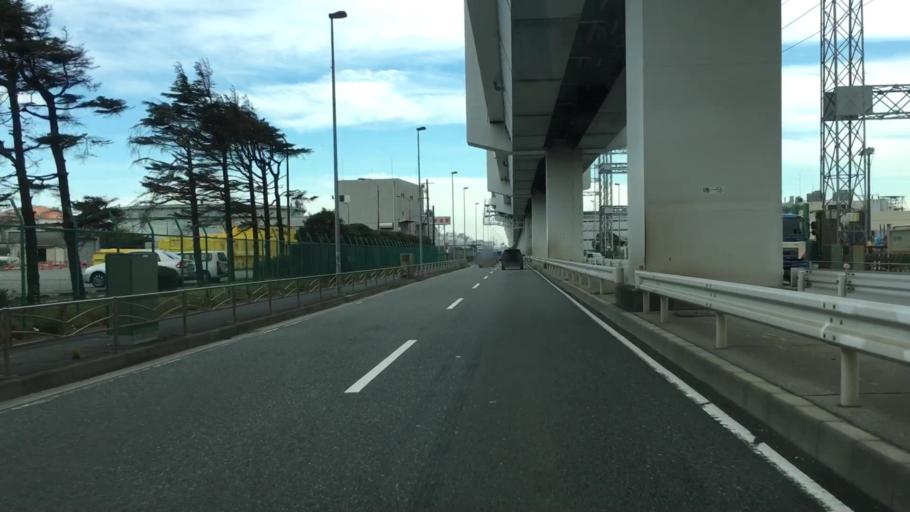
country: JP
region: Kanagawa
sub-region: Kawasaki-shi
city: Kawasaki
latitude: 35.5311
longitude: 139.7699
